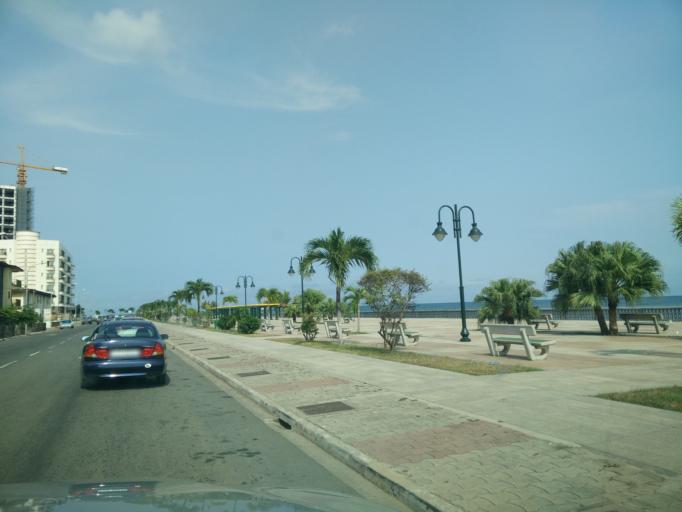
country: GQ
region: Litoral
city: Bata
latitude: 1.8669
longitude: 9.7644
